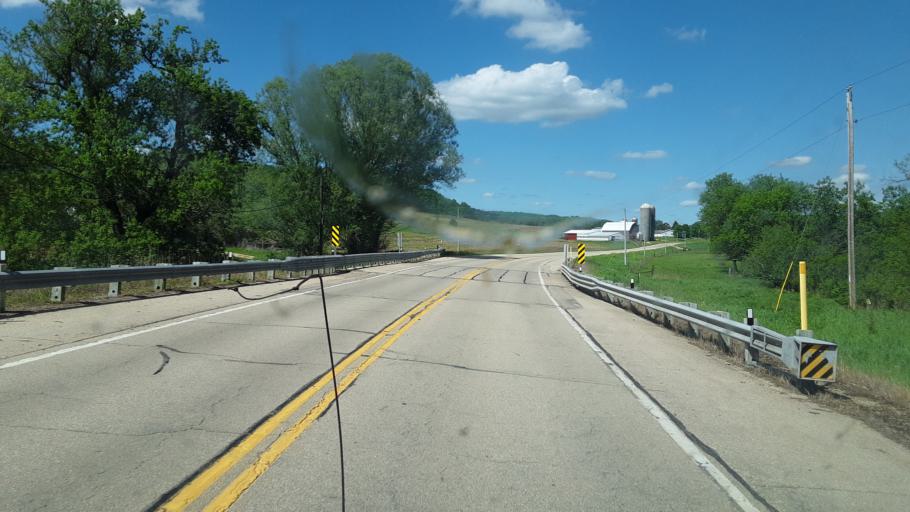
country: US
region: Wisconsin
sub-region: Richland County
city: Richland Center
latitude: 43.4374
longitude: -90.2422
